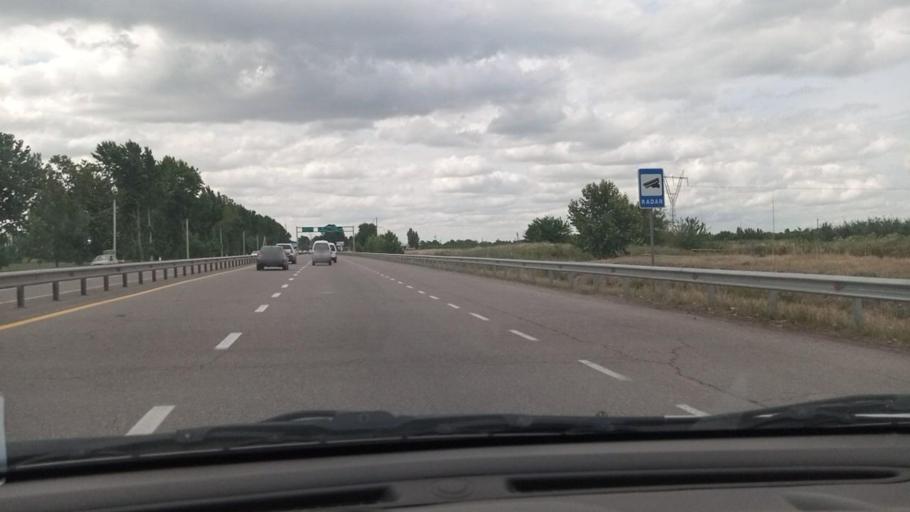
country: UZ
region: Toshkent Shahri
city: Bektemir
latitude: 41.1777
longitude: 69.4094
